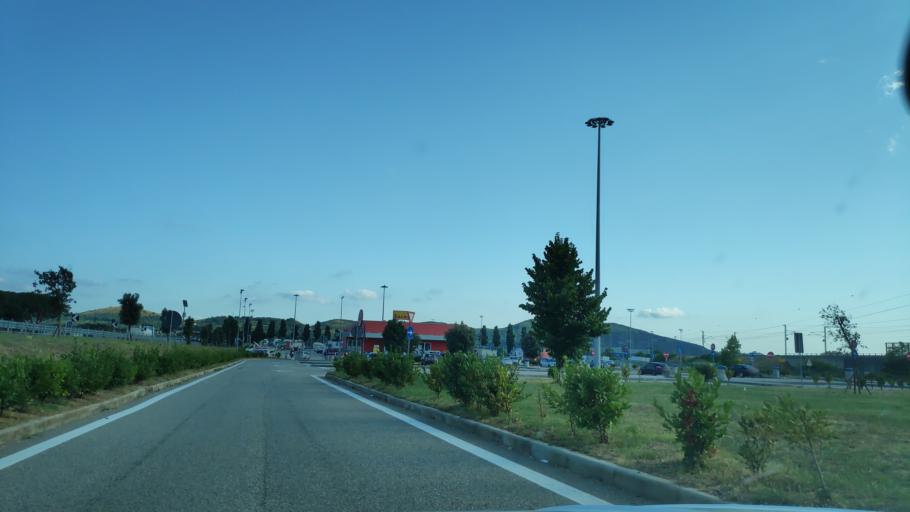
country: IT
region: Campania
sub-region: Provincia di Caserta
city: Teano
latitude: 41.2350
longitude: 14.0921
